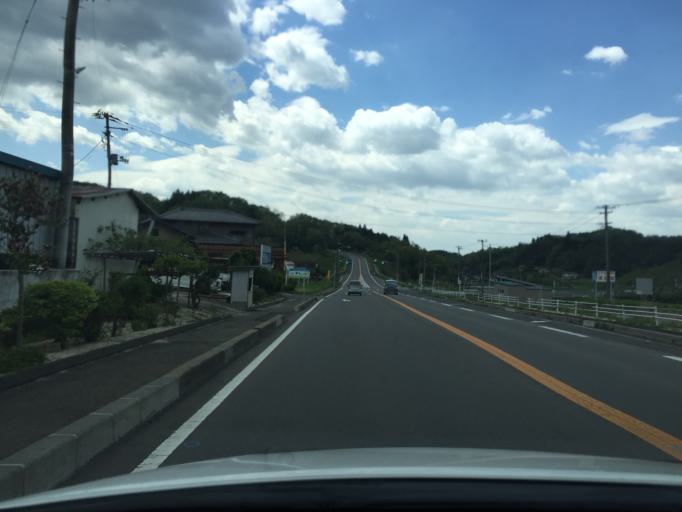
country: JP
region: Fukushima
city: Fukushima-shi
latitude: 37.6926
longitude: 140.5247
